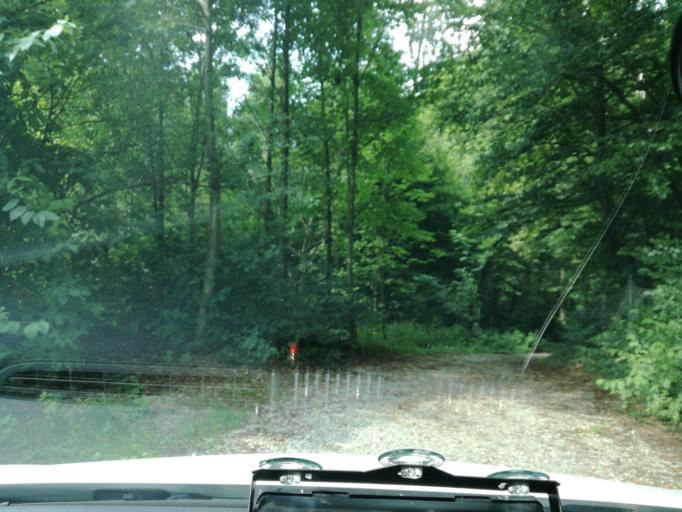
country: AT
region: Styria
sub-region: Politischer Bezirk Weiz
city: Gleisdorf
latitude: 47.1097
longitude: 15.7193
